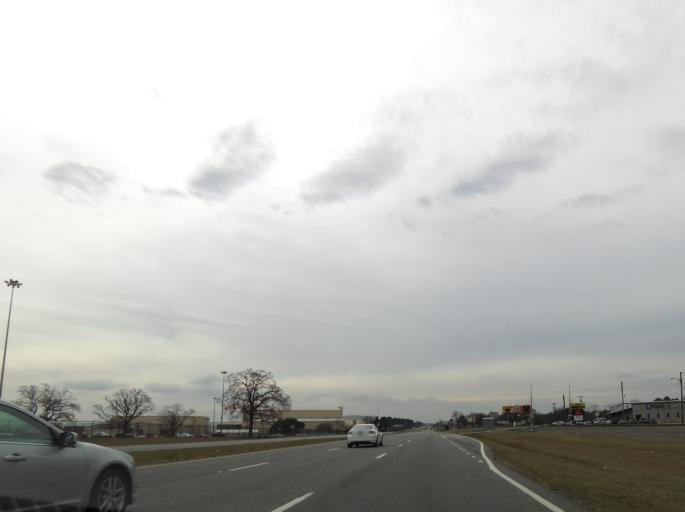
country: US
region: Georgia
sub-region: Houston County
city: Warner Robins
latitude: 32.6353
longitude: -83.6048
